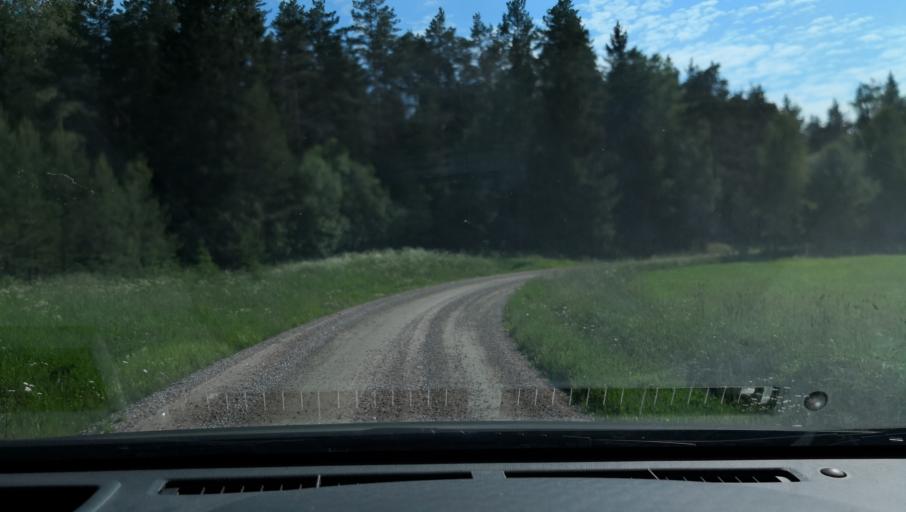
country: SE
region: Uppsala
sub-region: Enkopings Kommun
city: Orsundsbro
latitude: 59.8346
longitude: 17.2481
